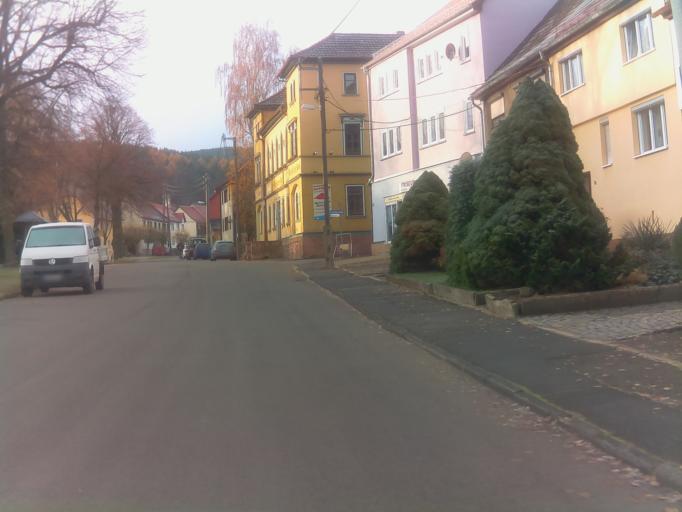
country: DE
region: Thuringia
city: Grafenhain
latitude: 50.8191
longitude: 10.7011
